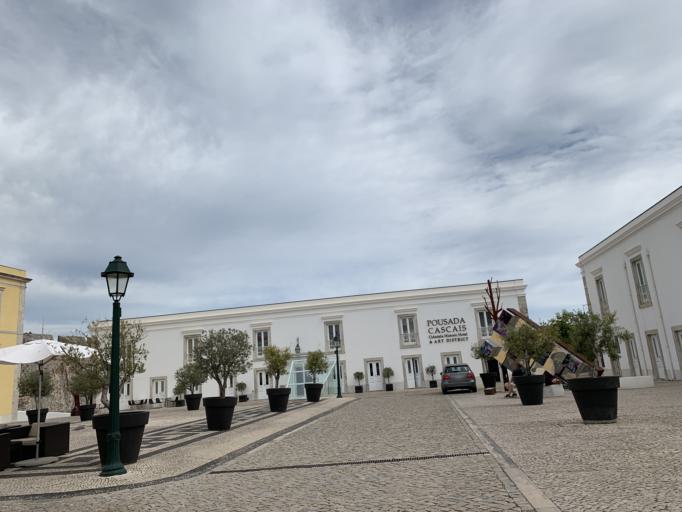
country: PT
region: Lisbon
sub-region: Cascais
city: Cascais
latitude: 38.6940
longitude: -9.4196
